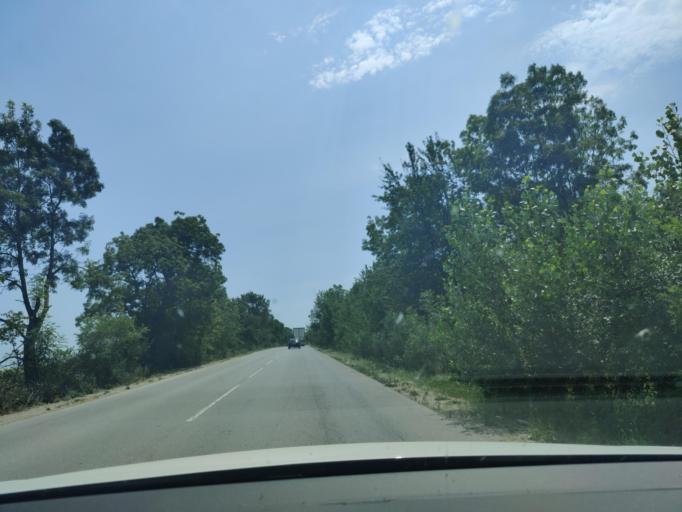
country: BG
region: Montana
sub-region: Obshtina Montana
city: Montana
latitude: 43.4673
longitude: 23.0871
